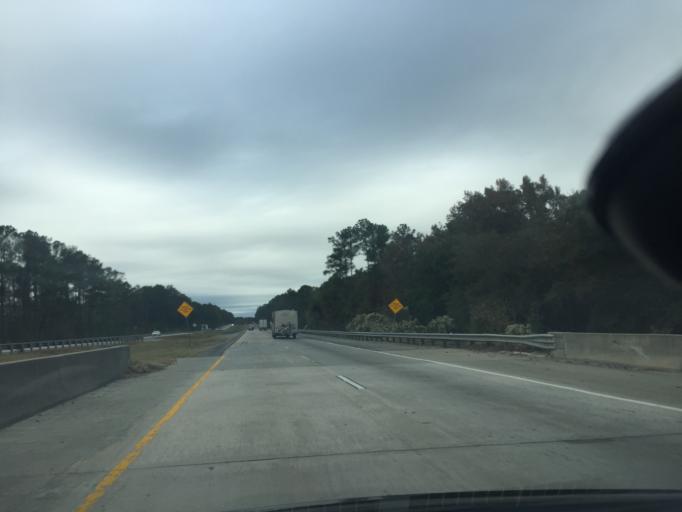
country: US
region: Georgia
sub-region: Chatham County
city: Bloomingdale
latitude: 32.1381
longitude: -81.4073
